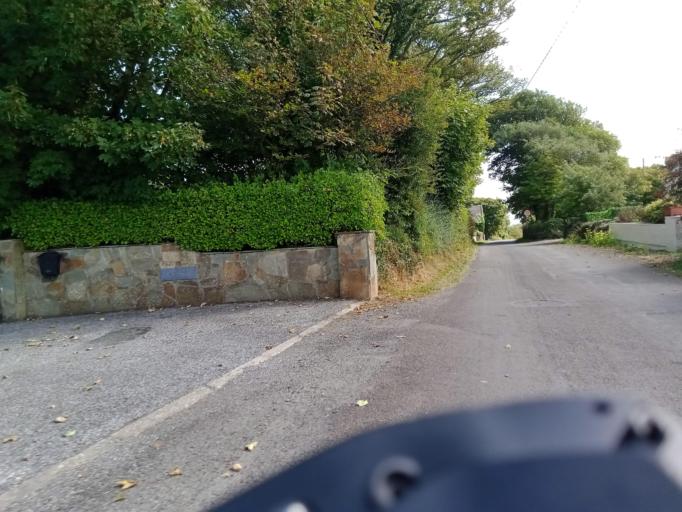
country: IE
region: Munster
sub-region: Waterford
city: Dungarvan
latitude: 52.1283
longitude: -7.4516
